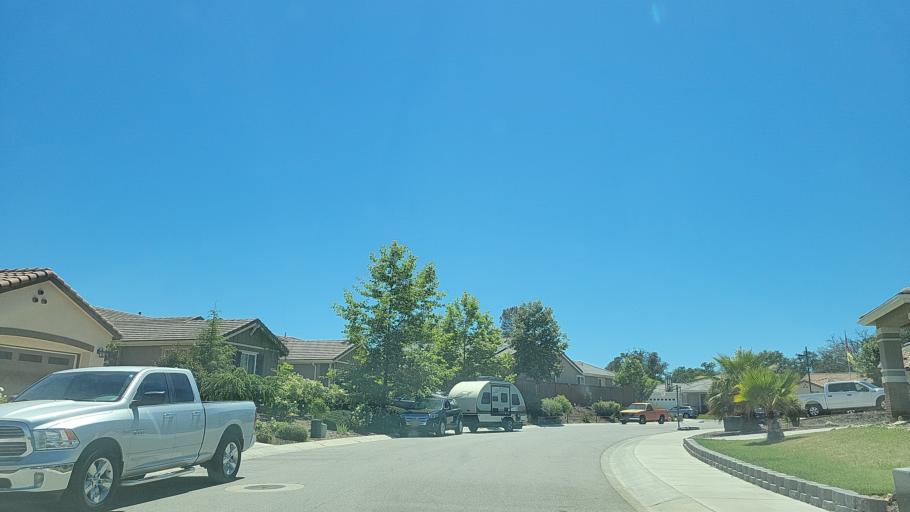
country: US
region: California
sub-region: San Luis Obispo County
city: Atascadero
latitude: 35.4508
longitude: -120.6272
